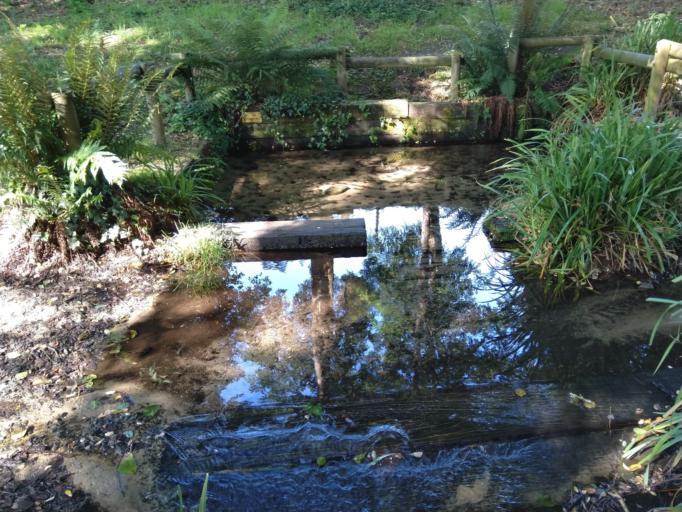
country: FR
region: Aquitaine
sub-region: Departement des Landes
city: Saint-Paul-les-Dax
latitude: 43.7331
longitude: -1.0732
